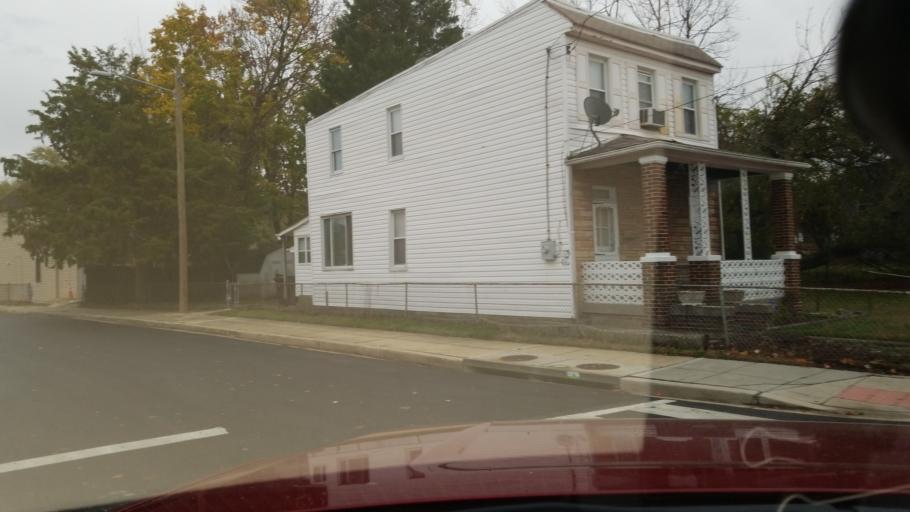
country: US
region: Maryland
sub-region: Prince George's County
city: Fairmount Heights
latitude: 38.9048
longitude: -76.9362
